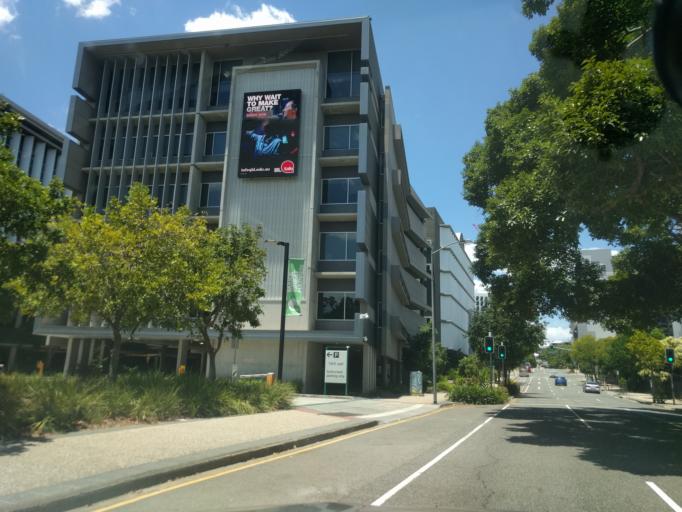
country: AU
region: Queensland
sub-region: Brisbane
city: South Brisbane
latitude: -27.4790
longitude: 153.0192
